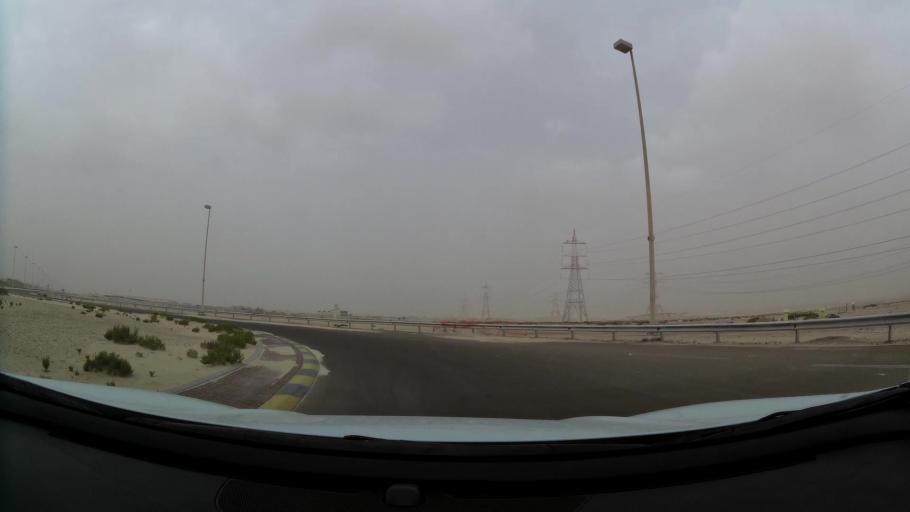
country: AE
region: Abu Dhabi
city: Abu Dhabi
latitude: 24.4314
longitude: 54.7536
